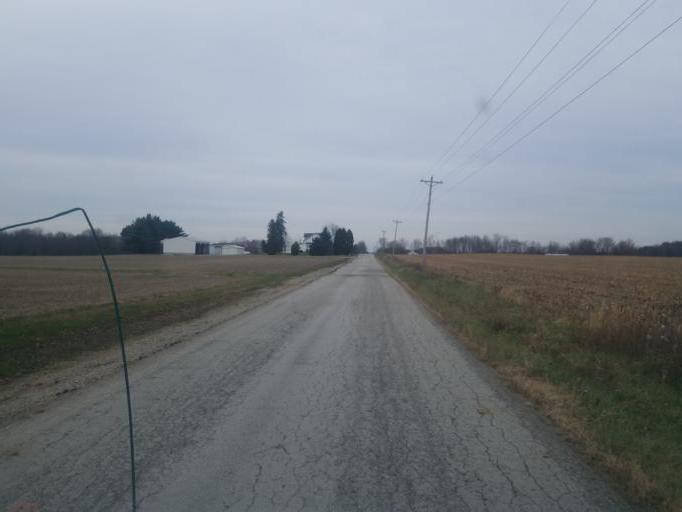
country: US
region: Ohio
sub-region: Knox County
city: Centerburg
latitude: 40.3830
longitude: -82.6536
